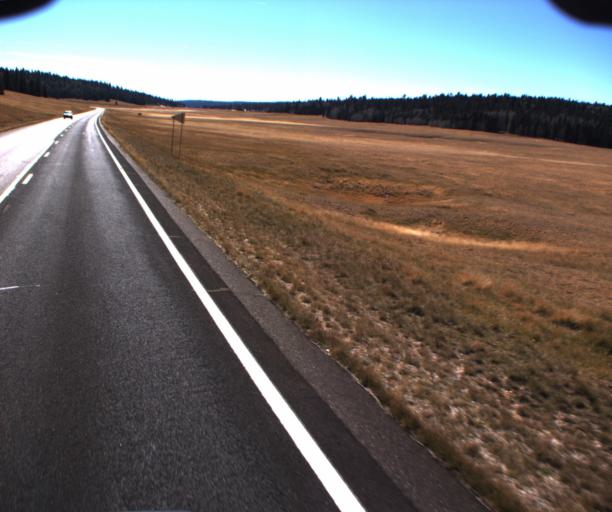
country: US
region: Arizona
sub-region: Coconino County
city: Grand Canyon
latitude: 36.4324
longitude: -112.1330
